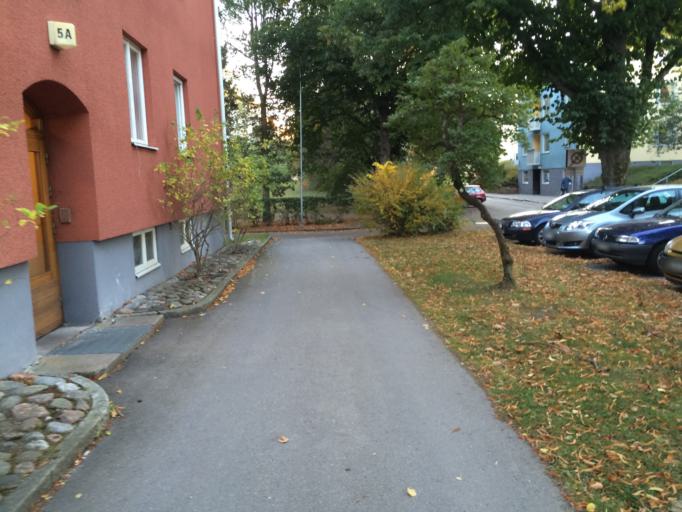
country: SE
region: Gaevleborg
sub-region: Gavle Kommun
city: Gavle
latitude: 60.6704
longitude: 17.1433
